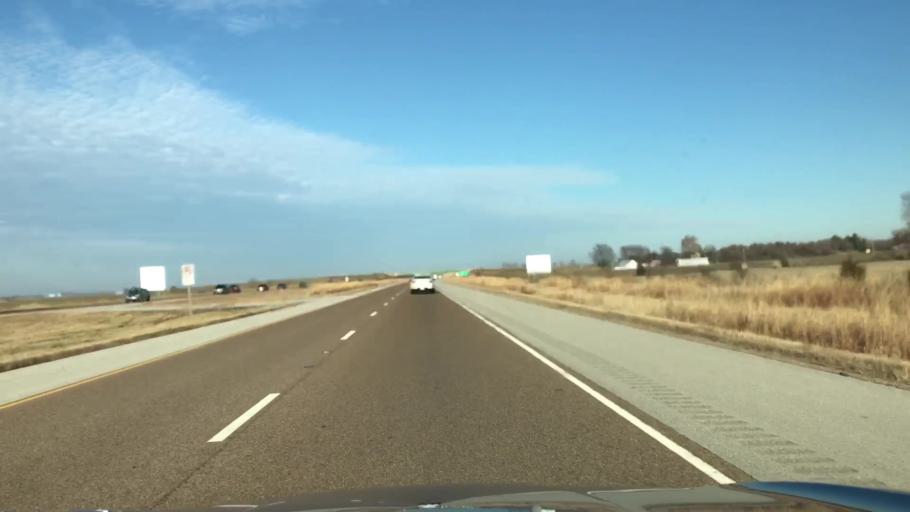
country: US
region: Illinois
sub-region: Montgomery County
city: Litchfield
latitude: 39.1848
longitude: -89.6752
